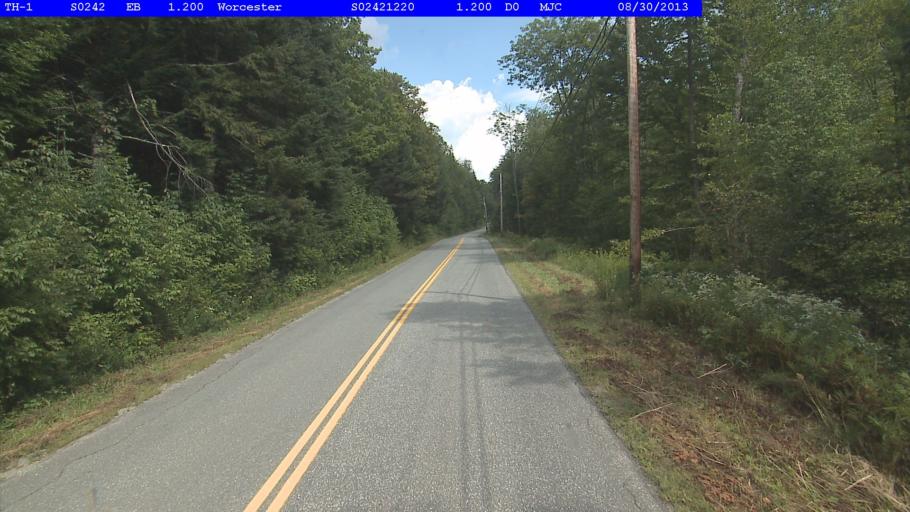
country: US
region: Vermont
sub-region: Washington County
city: Montpelier
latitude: 44.3828
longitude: -72.5335
